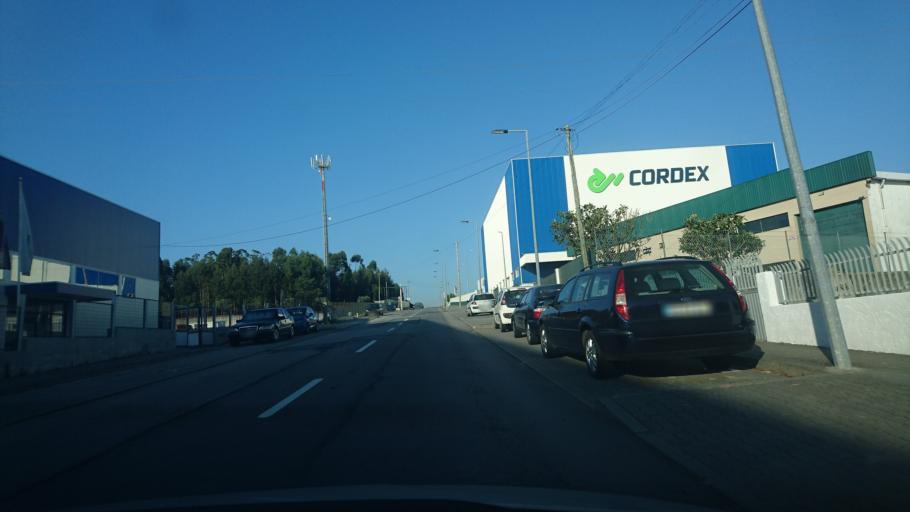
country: PT
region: Aveiro
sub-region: Ovar
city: Esmoriz
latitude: 40.9659
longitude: -8.6170
